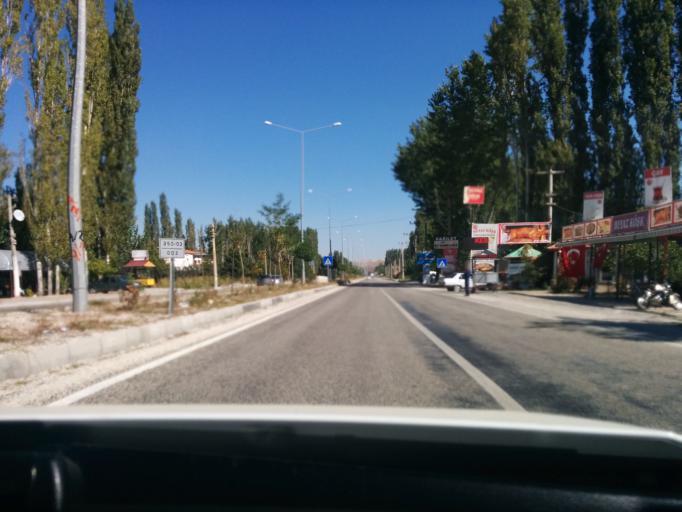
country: TR
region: Antalya
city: Kizilcadag
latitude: 37.0230
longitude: 29.8219
